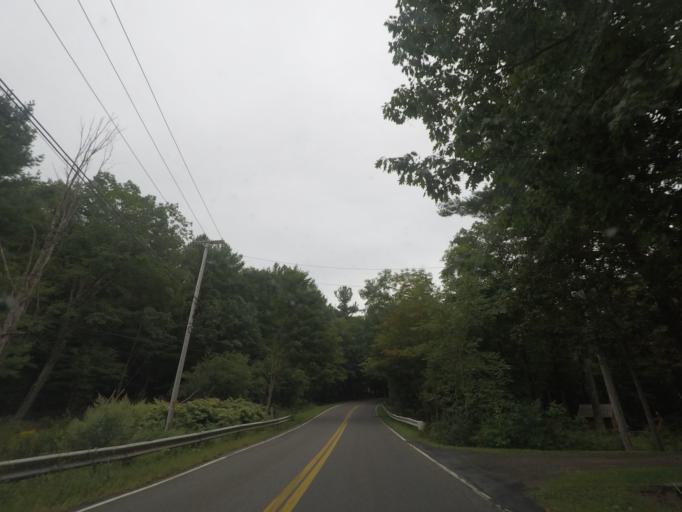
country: US
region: New York
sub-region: Columbia County
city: Chatham
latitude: 42.4193
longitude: -73.5427
